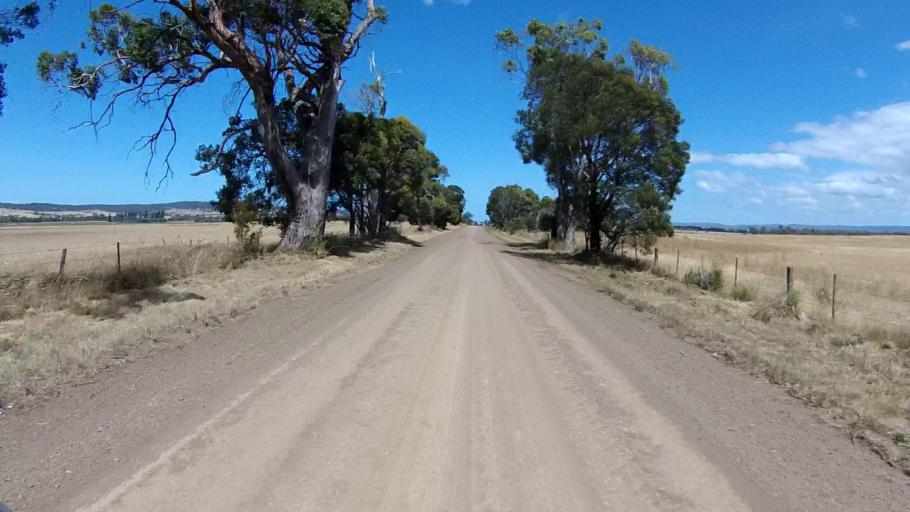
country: AU
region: Tasmania
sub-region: Break O'Day
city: St Helens
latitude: -41.9908
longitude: 148.0669
